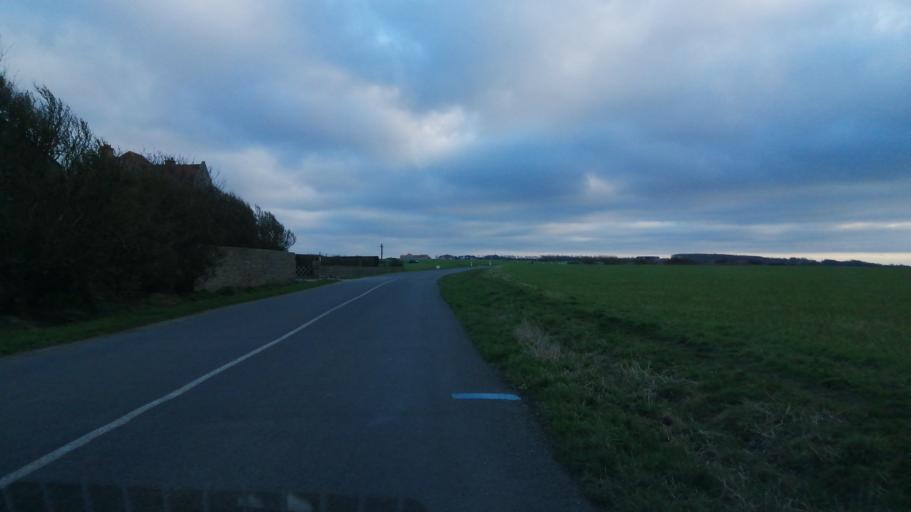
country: FR
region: Nord-Pas-de-Calais
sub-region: Departement du Pas-de-Calais
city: Ambleteuse
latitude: 50.8541
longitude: 1.5928
